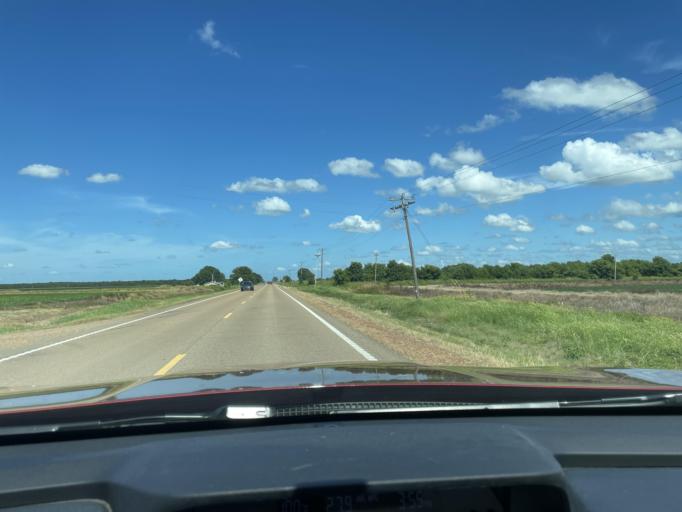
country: US
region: Mississippi
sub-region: Humphreys County
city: Belzoni
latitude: 33.1828
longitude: -90.6491
